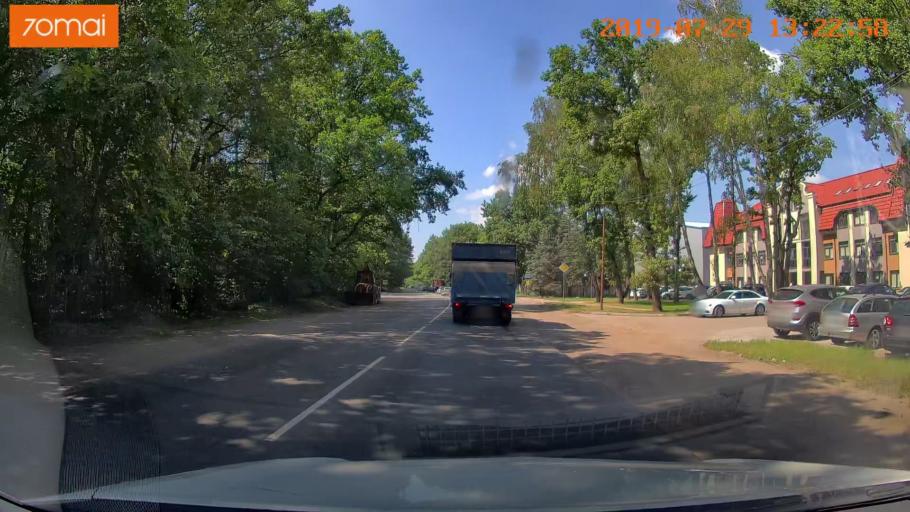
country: RU
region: Kaliningrad
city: Vzmorye
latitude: 54.7149
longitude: 20.3635
